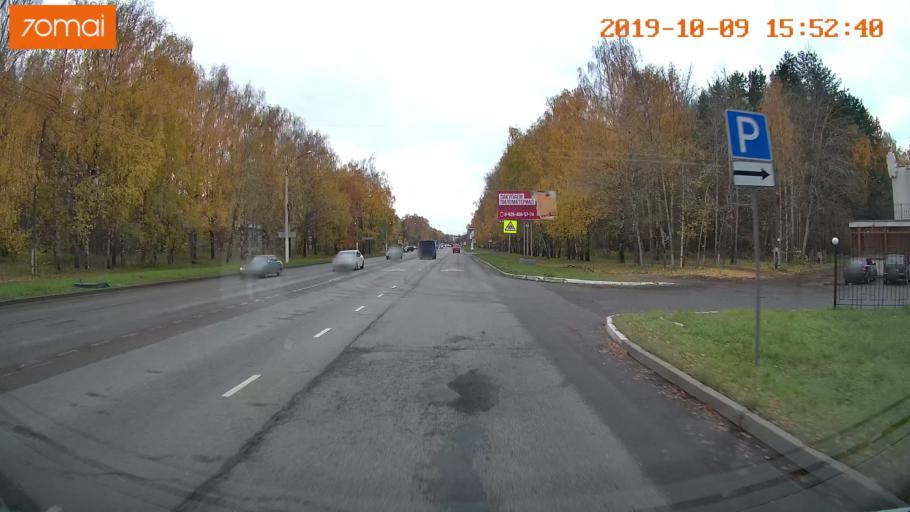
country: RU
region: Kostroma
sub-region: Kostromskoy Rayon
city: Kostroma
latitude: 57.7878
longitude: 40.9652
